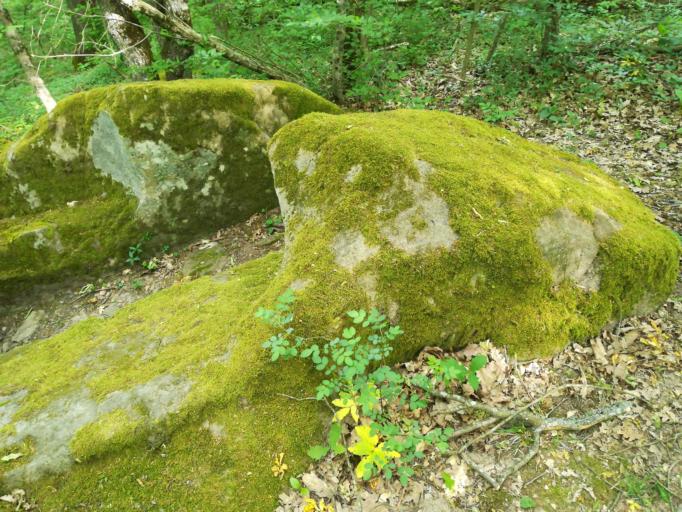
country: RU
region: Krasnodarskiy
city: Azovskaya
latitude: 44.6345
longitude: 38.6217
